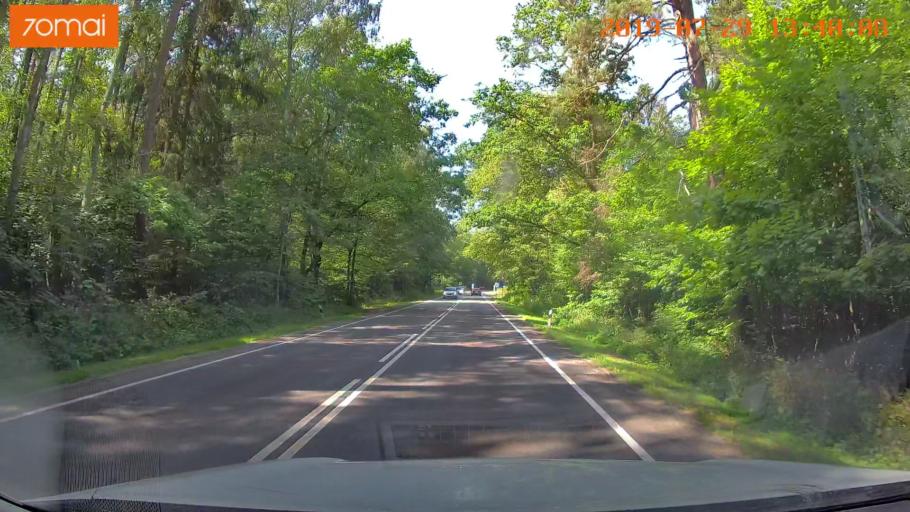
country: RU
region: Kaliningrad
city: Svetlyy
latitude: 54.7264
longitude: 20.1420
